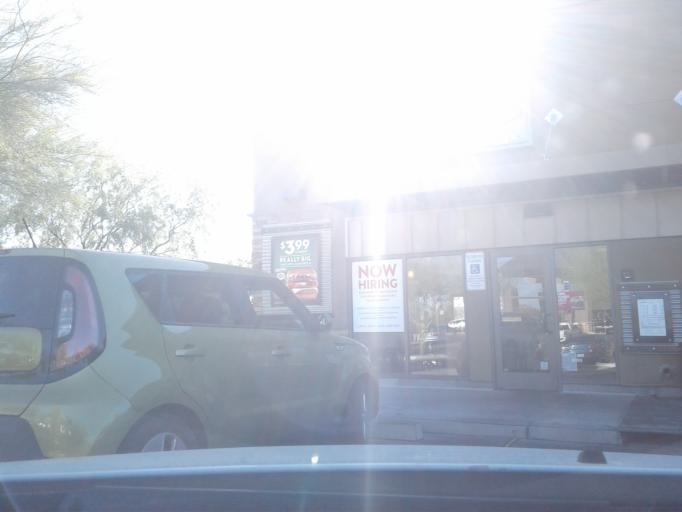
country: US
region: Arizona
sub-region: Maricopa County
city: Anthem
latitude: 33.7979
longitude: -112.1167
